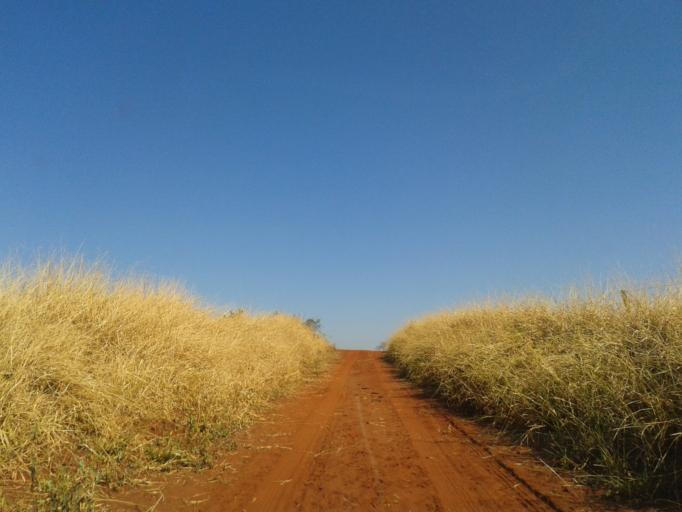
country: BR
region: Minas Gerais
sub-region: Santa Vitoria
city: Santa Vitoria
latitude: -19.0473
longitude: -49.9414
